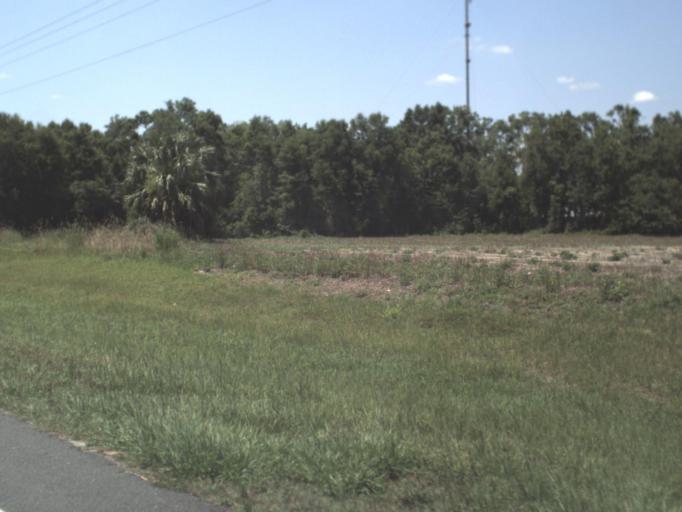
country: US
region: Florida
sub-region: Lafayette County
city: Mayo
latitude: 30.0701
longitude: -83.2016
